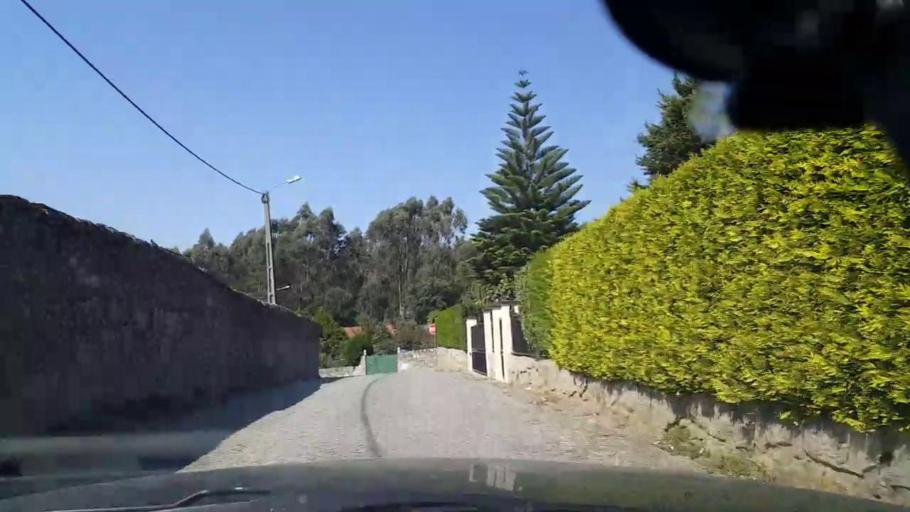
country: PT
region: Porto
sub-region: Vila do Conde
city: Arvore
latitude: 41.3807
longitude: -8.7061
